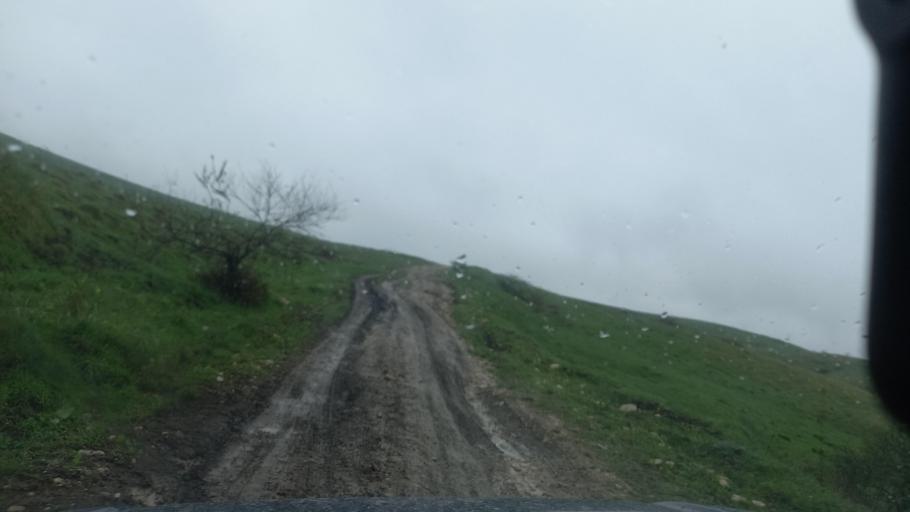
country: RU
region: Kabardino-Balkariya
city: Kamennomostskoye
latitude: 43.6873
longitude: 42.9924
